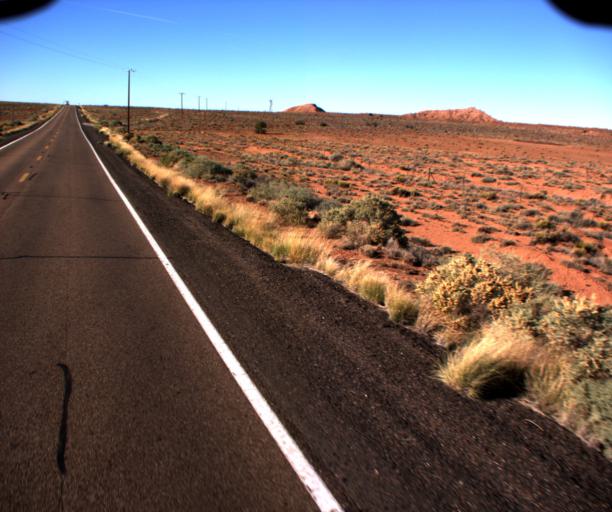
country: US
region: Arizona
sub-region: Navajo County
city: Holbrook
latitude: 34.8529
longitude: -110.1722
